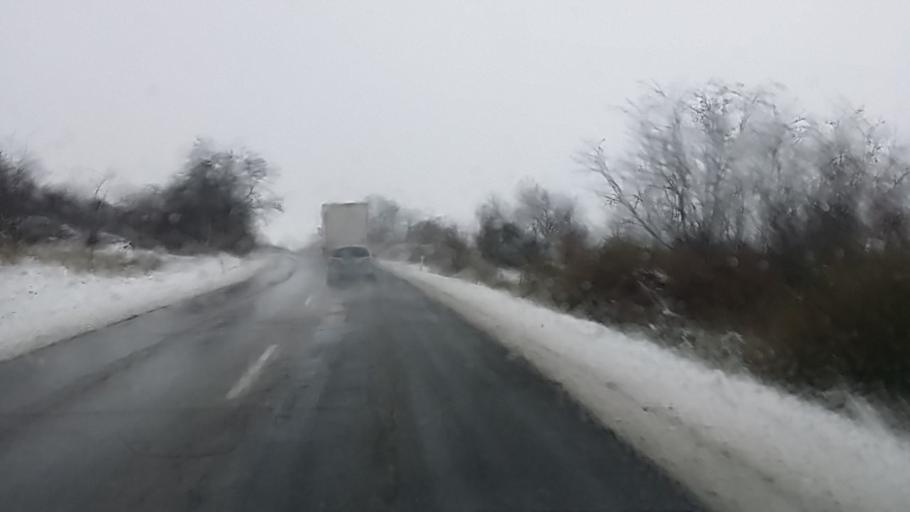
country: HU
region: Komarom-Esztergom
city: Acs
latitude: 47.7263
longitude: 18.0079
